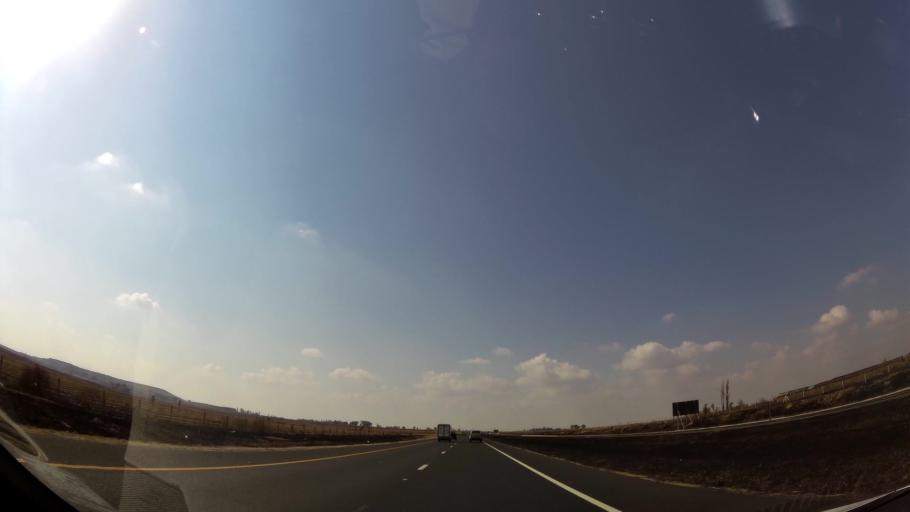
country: ZA
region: Gauteng
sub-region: Ekurhuleni Metropolitan Municipality
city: Springs
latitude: -26.1637
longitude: 28.5037
